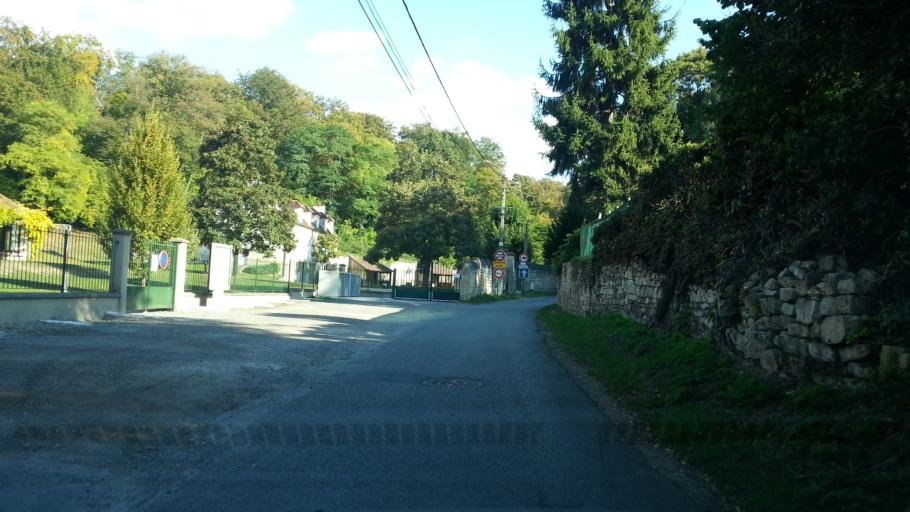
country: FR
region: Picardie
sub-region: Departement de l'Oise
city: Saint-Maximin
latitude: 49.2256
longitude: 2.4467
